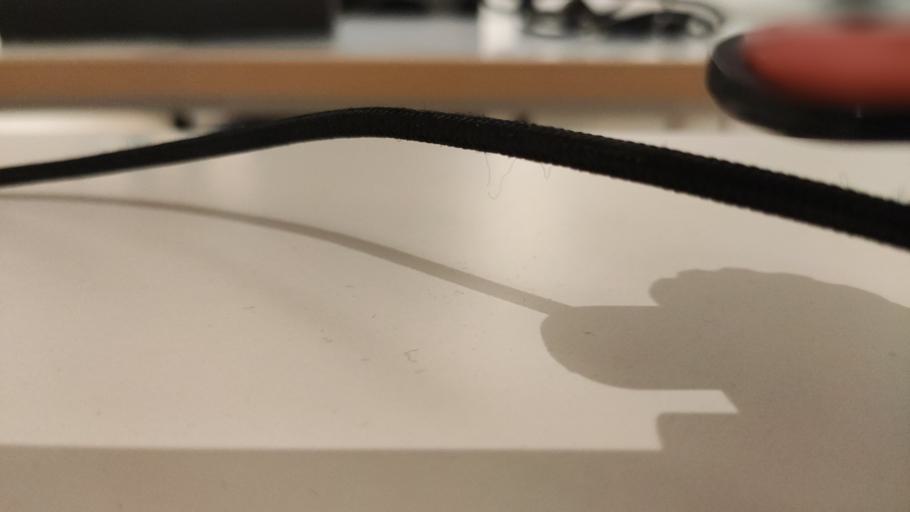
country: RU
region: Moskovskaya
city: Dorokhovo
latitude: 55.4956
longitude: 36.3492
